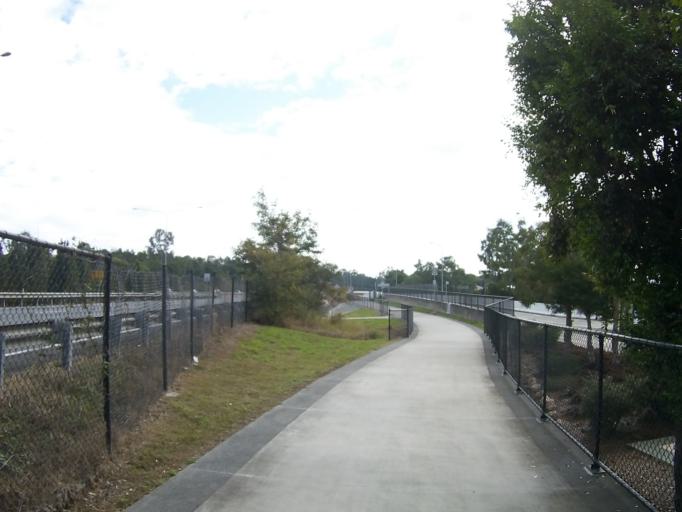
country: AU
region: Queensland
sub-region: Brisbane
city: Annerley
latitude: -27.5109
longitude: 153.0400
